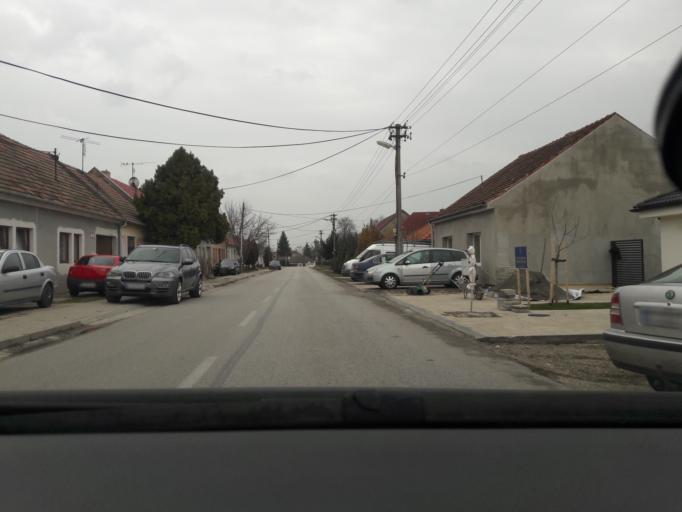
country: SK
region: Bratislavsky
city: Senec
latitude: 48.3126
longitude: 17.4414
